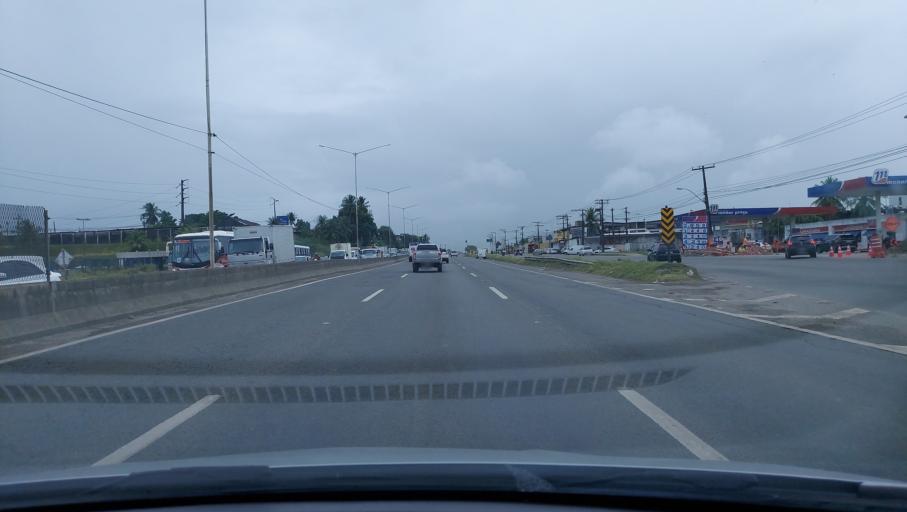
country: BR
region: Bahia
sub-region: Salvador
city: Salvador
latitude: -12.8954
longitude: -38.4481
